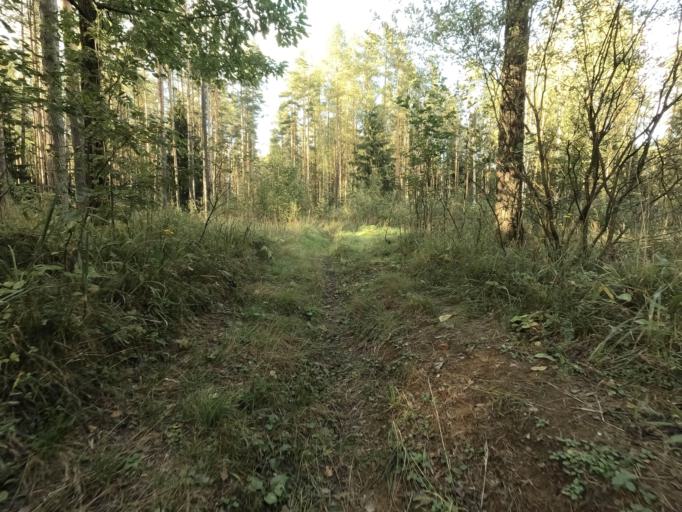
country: RU
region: Leningrad
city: Imeni Sverdlova
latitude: 59.8474
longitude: 30.7283
